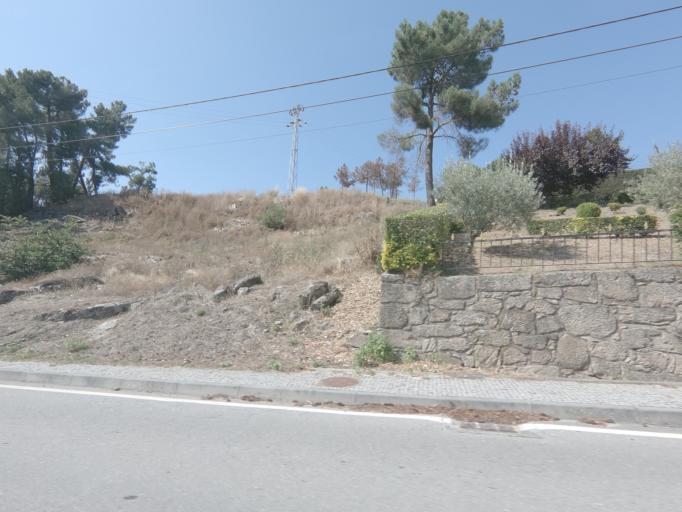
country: PT
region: Viseu
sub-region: Tarouca
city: Tarouca
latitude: 41.0227
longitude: -7.7506
